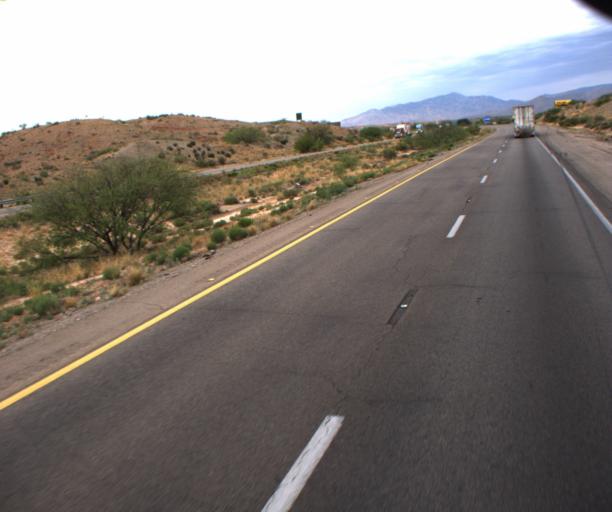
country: US
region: Arizona
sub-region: Cochise County
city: Benson
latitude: 31.9746
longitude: -110.2876
